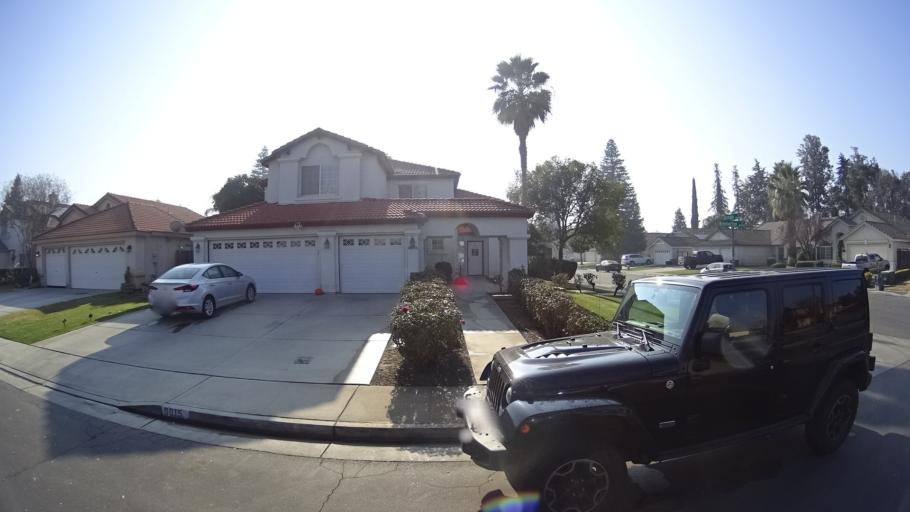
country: US
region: California
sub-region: Kern County
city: Greenacres
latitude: 35.3952
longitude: -119.1026
